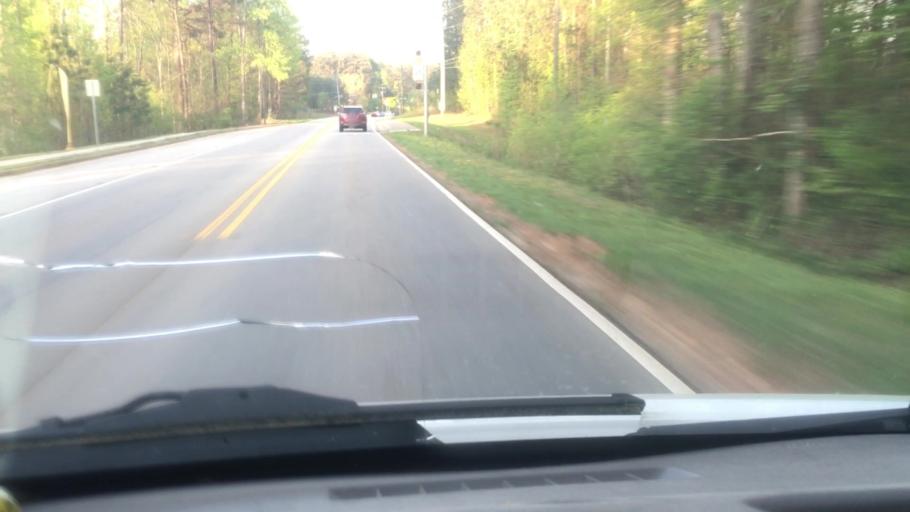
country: US
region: Georgia
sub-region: Paulding County
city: Hiram
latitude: 33.9398
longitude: -84.7495
